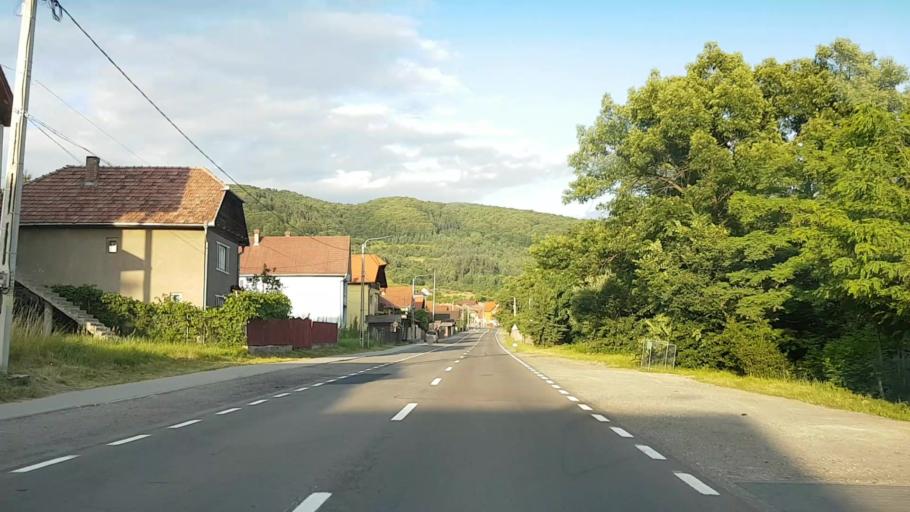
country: RO
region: Harghita
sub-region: Comuna Corund
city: Corund
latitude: 46.4701
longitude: 25.1913
